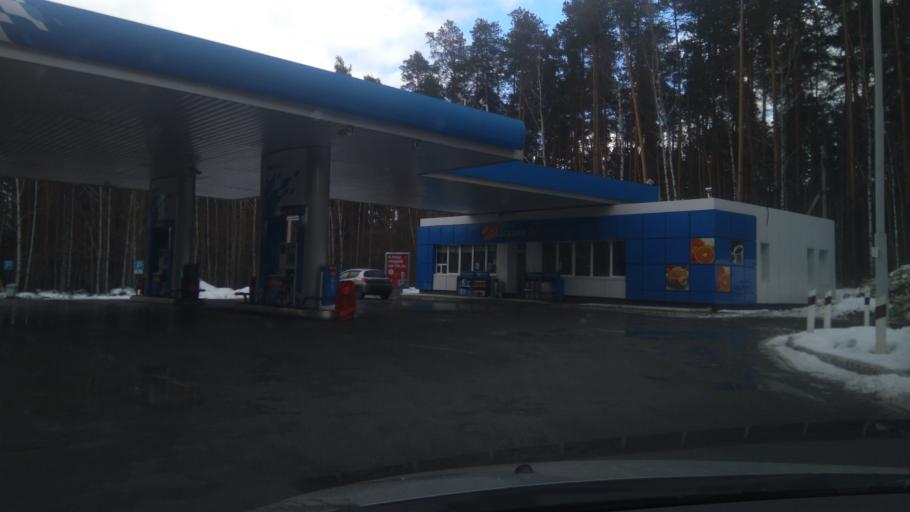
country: RU
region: Sverdlovsk
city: Shirokaya Rechka
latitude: 56.8246
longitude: 60.4677
